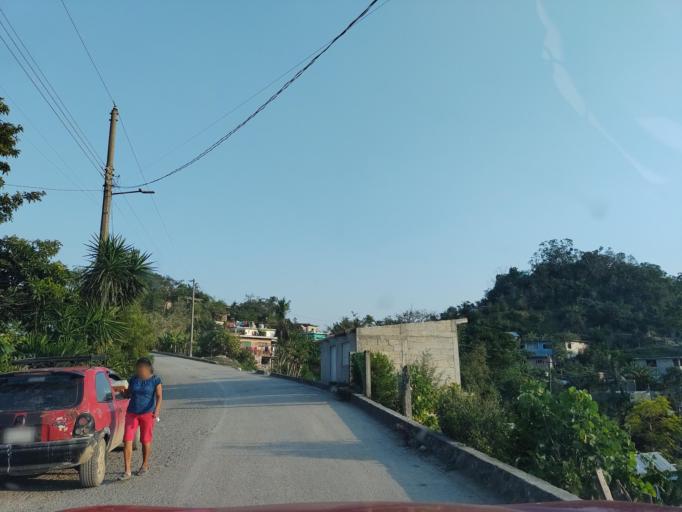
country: MX
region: Veracruz
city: Agua Dulce
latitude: 20.4048
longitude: -97.2898
